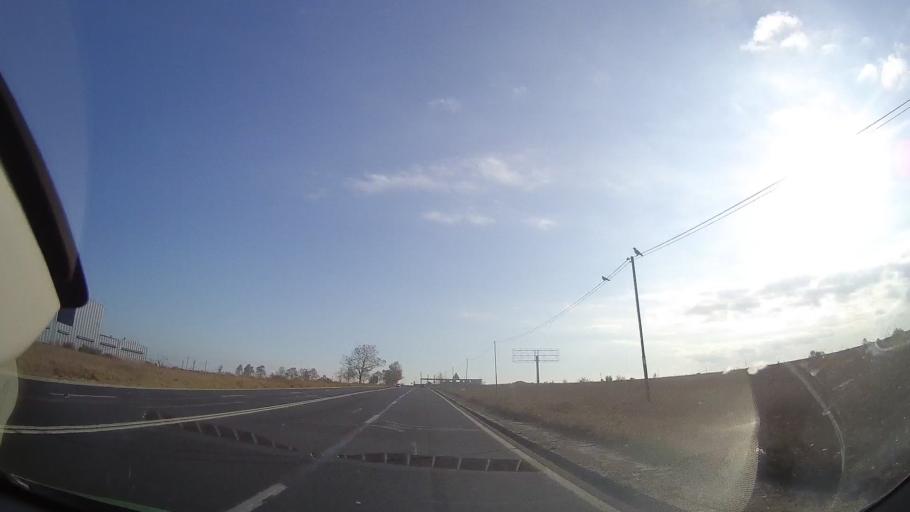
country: RO
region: Constanta
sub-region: Municipiul Mangalia
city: Mangalia
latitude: 43.7966
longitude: 28.5597
